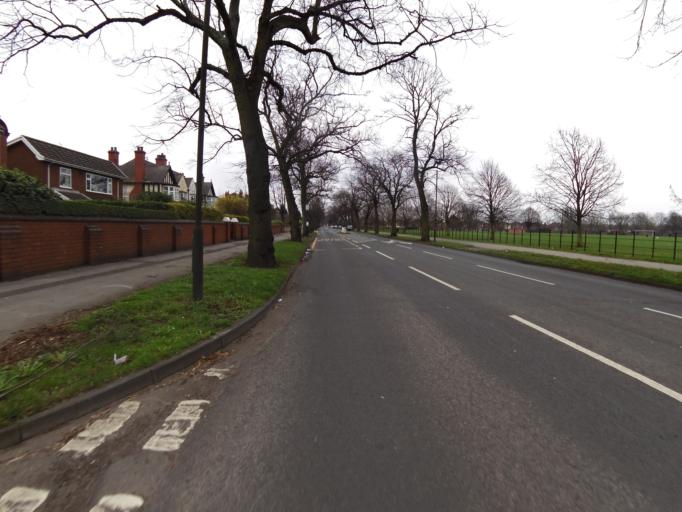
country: GB
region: England
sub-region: Doncaster
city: Doncaster
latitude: 53.5254
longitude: -1.1145
